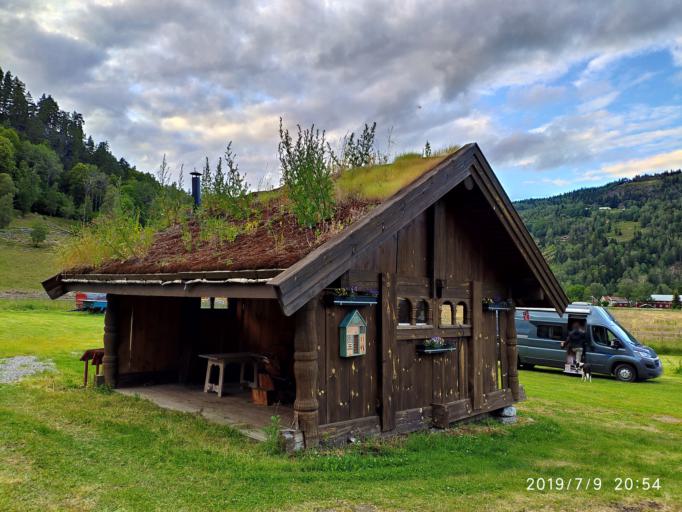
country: NO
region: Telemark
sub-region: Seljord
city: Seljord
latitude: 59.5603
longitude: 8.5637
